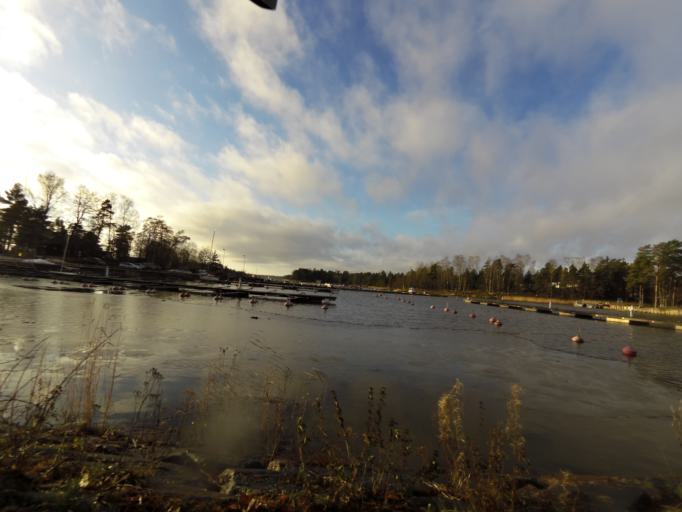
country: FI
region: Uusimaa
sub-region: Helsinki
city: Koukkuniemi
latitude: 60.1552
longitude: 24.7731
